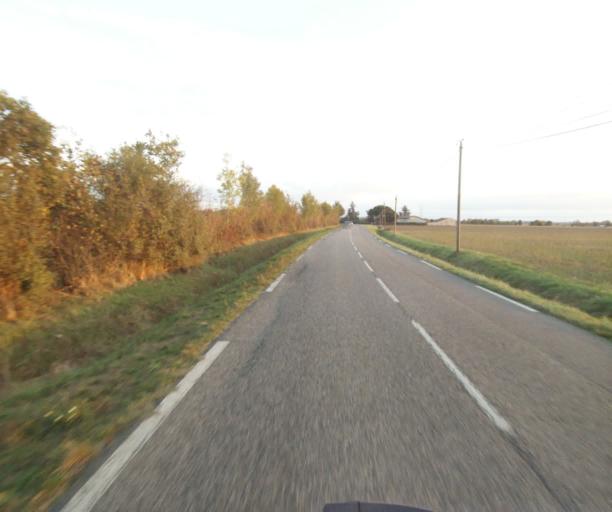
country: FR
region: Midi-Pyrenees
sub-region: Departement du Tarn-et-Garonne
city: Verdun-sur-Garonne
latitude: 43.8340
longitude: 1.2406
